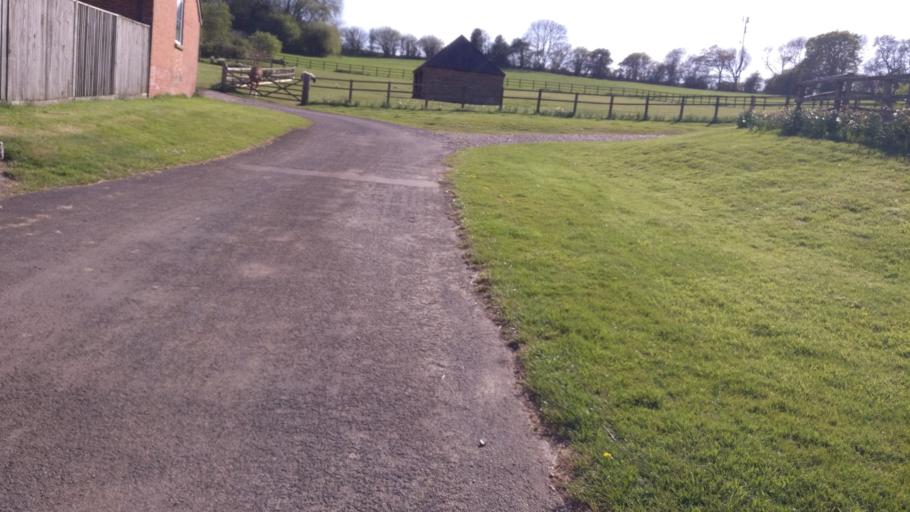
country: GB
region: England
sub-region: Hampshire
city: Basingstoke
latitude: 51.2279
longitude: -1.0770
